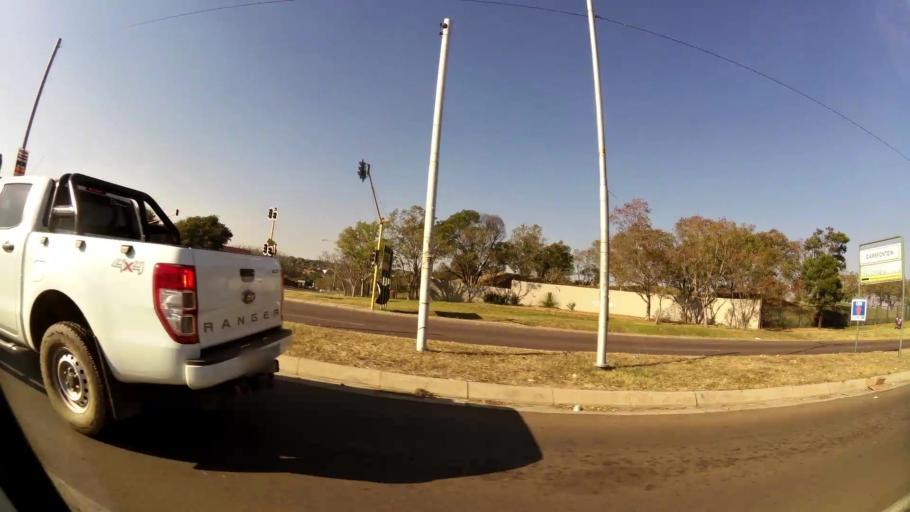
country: ZA
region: Gauteng
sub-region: City of Tshwane Metropolitan Municipality
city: Centurion
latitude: -25.8135
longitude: 28.3033
